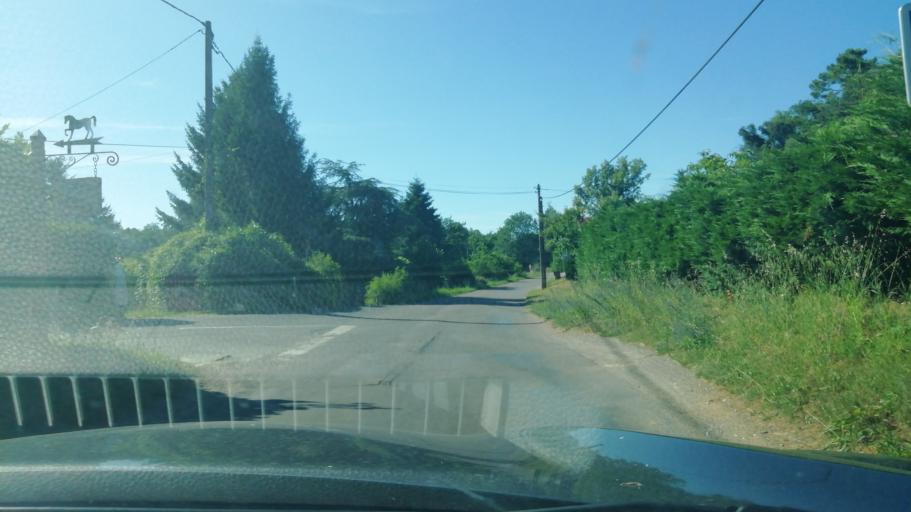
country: FR
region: Aquitaine
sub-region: Departement de la Dordogne
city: Sarlat-la-Caneda
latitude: 44.8638
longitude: 1.2232
